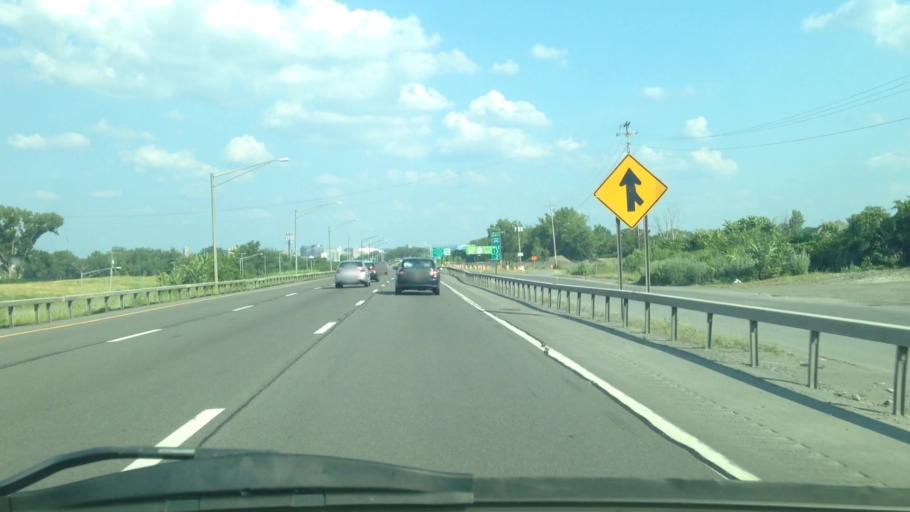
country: US
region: New York
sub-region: Onondaga County
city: Solvay
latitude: 43.0641
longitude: -76.1945
